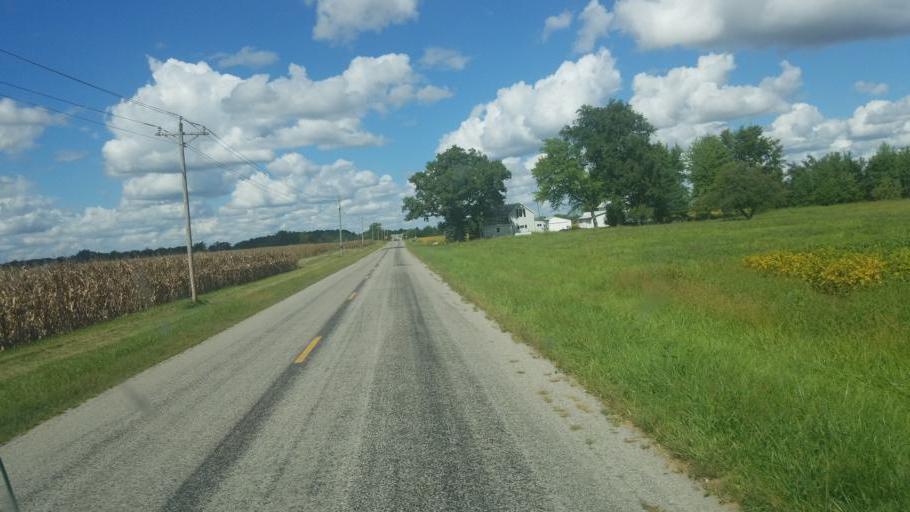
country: US
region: Ohio
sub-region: Champaign County
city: North Lewisburg
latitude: 40.4052
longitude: -83.5007
